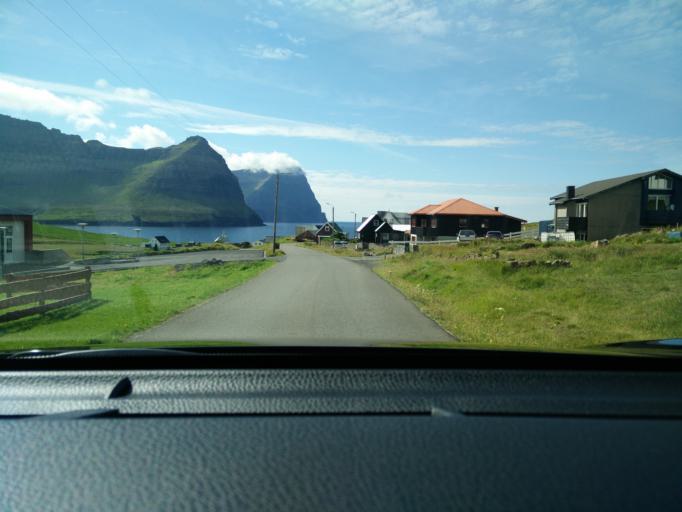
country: FO
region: Nordoyar
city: Klaksvik
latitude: 62.3602
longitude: -6.5338
